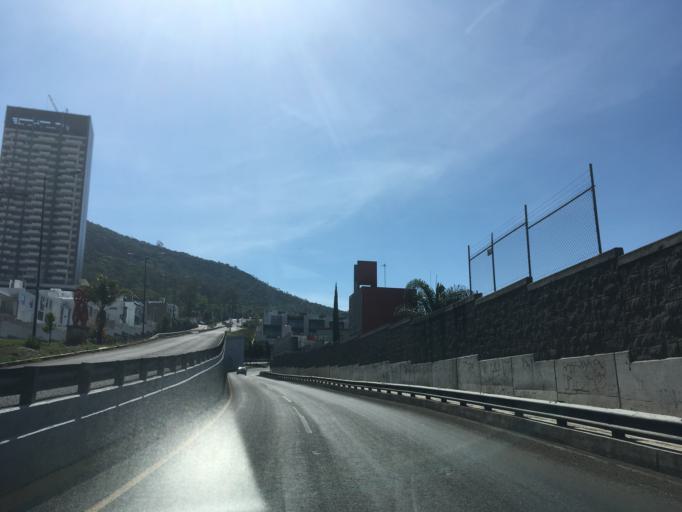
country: MX
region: Michoacan
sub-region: Morelia
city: Puerto de Buenavista (Lazaro Cardenas)
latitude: 19.6920
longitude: -101.1431
